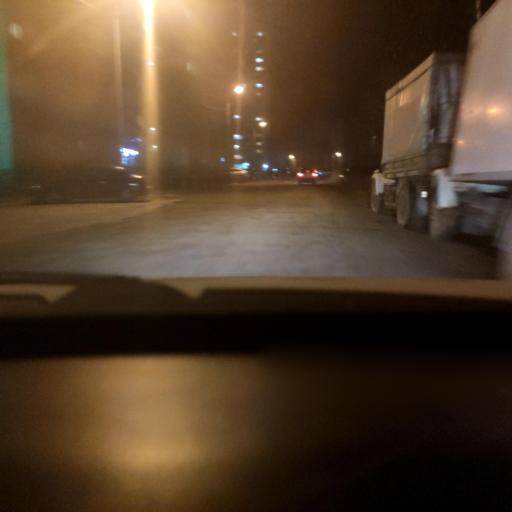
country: RU
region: Perm
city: Polazna
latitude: 58.1326
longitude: 56.3941
